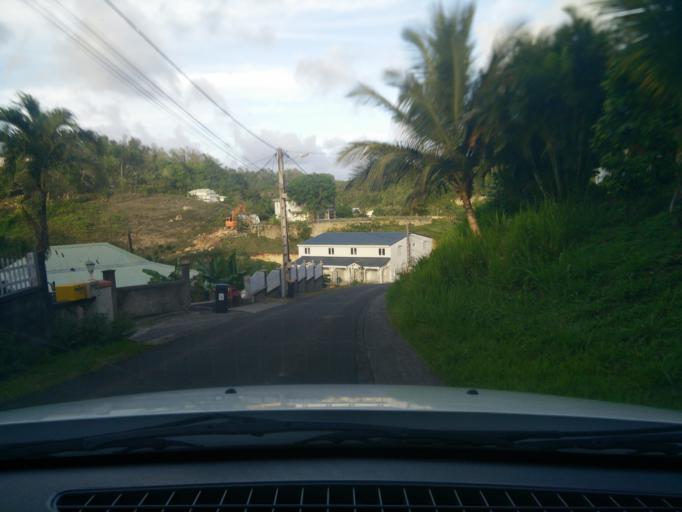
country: GP
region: Guadeloupe
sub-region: Guadeloupe
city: Les Abymes
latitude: 16.2492
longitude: -61.4951
